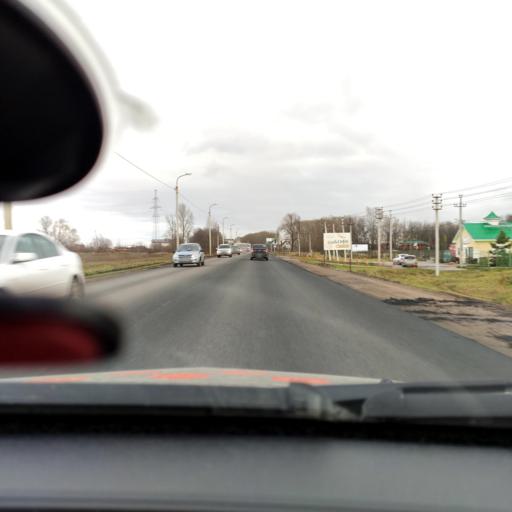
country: RU
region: Bashkortostan
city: Kabakovo
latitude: 54.6356
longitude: 56.0941
